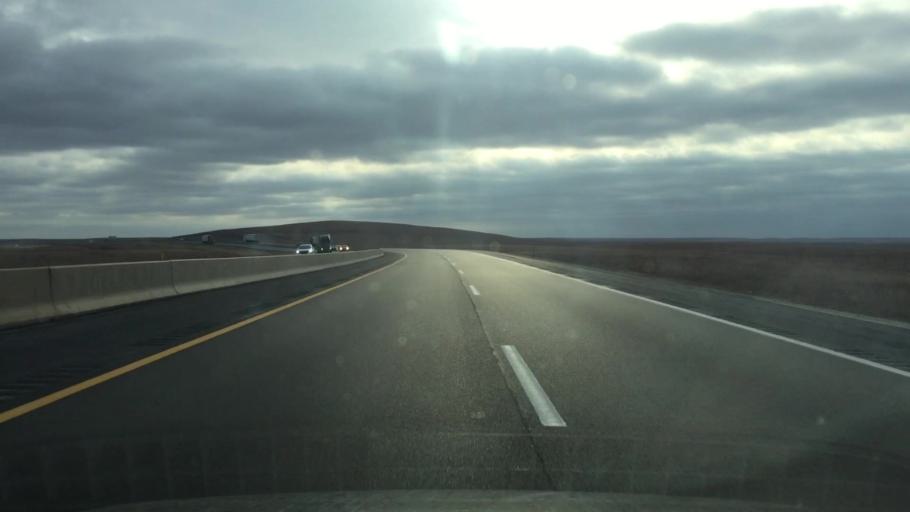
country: US
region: Kansas
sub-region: Chase County
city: Cottonwood Falls
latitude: 38.2202
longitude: -96.4323
